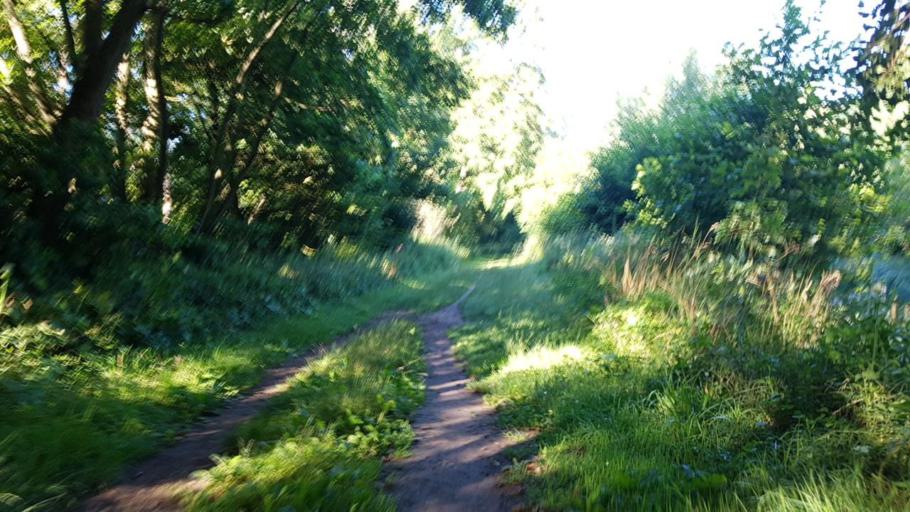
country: FR
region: Picardie
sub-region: Departement de l'Aisne
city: Essomes-sur-Marne
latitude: 49.0184
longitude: 3.3791
